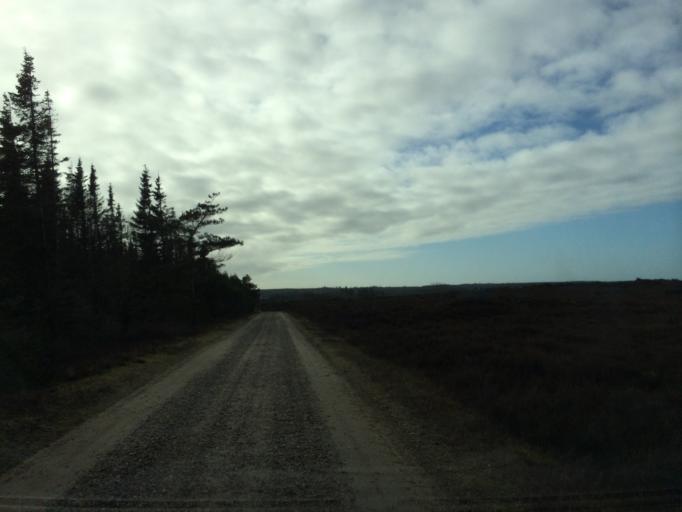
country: DK
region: Central Jutland
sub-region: Holstebro Kommune
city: Ulfborg
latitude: 56.2557
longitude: 8.4255
